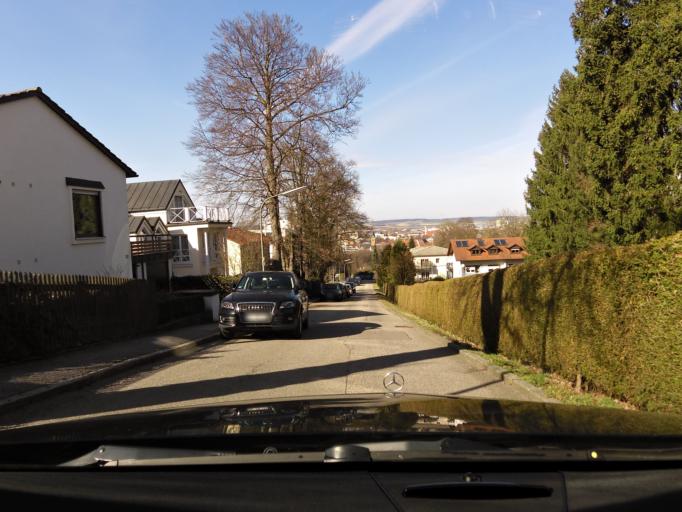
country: DE
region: Bavaria
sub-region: Lower Bavaria
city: Landshut
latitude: 48.5272
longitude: 12.1477
